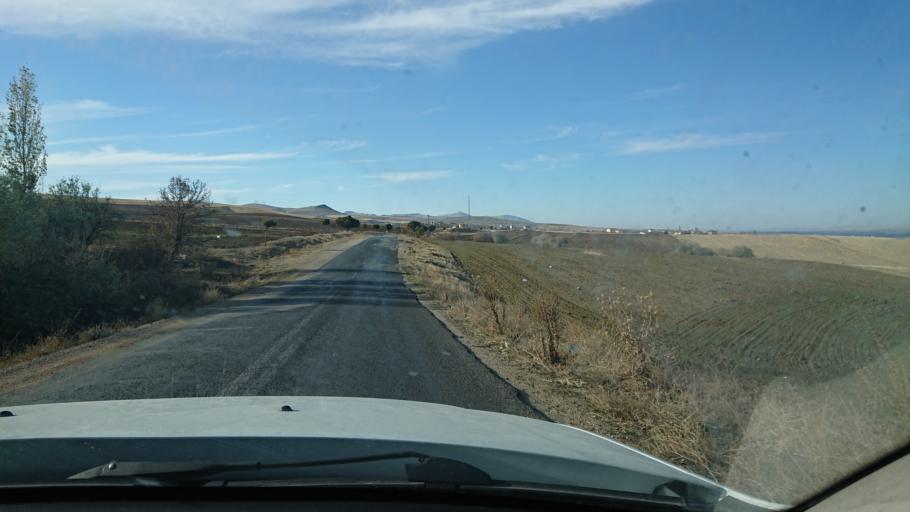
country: TR
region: Aksaray
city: Sariyahsi
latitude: 38.9724
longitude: 33.8626
